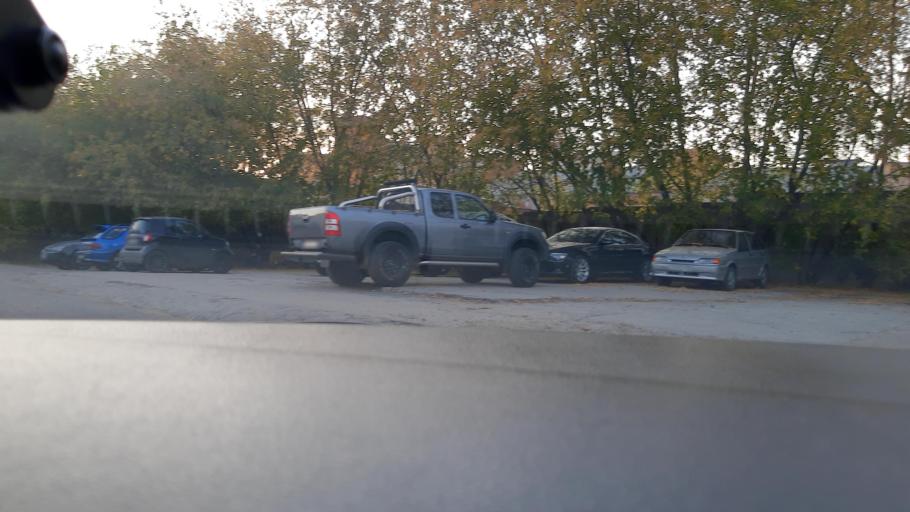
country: RU
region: Moskovskaya
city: Bol'shaya Setun'
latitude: 55.7048
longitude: 37.4075
